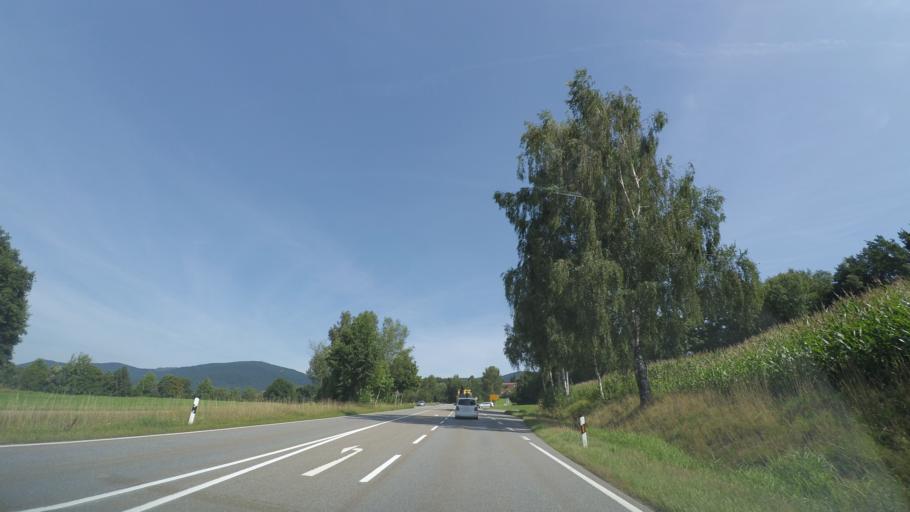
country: DE
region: Bavaria
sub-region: Lower Bavaria
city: Arnbruck
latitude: 49.1198
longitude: 12.9983
